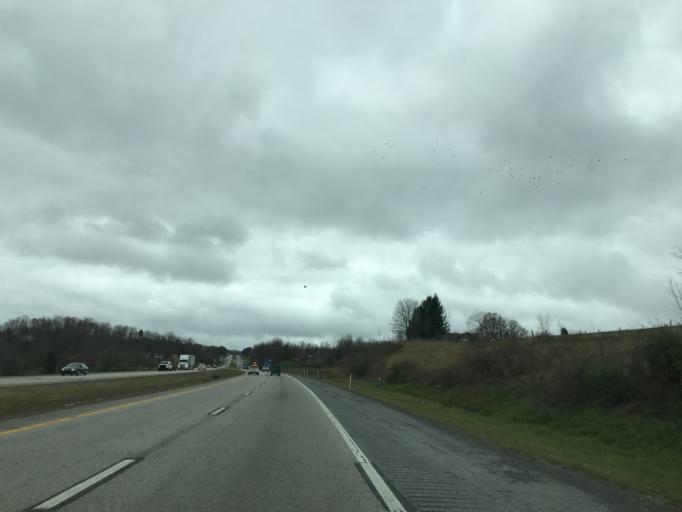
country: US
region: West Virginia
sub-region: Fayette County
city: Fayetteville
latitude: 38.0424
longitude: -81.1227
